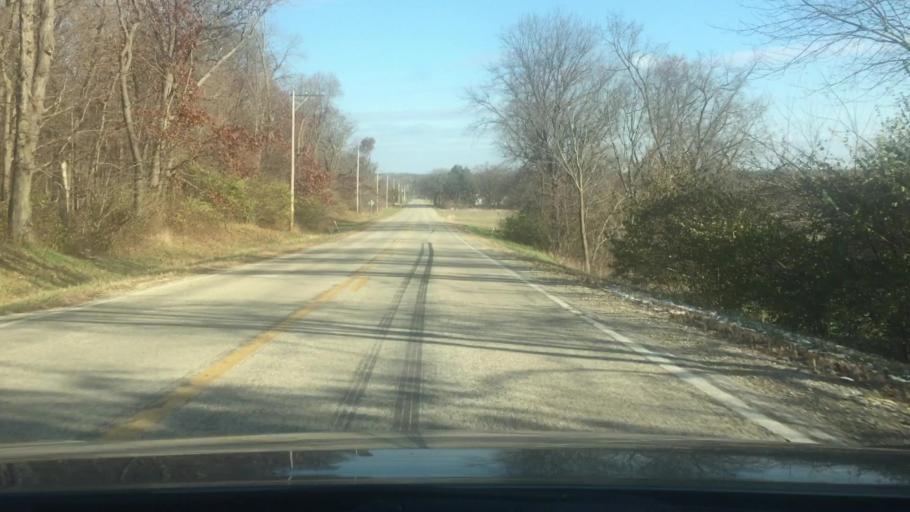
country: US
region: Wisconsin
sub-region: Jefferson County
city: Palmyra
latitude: 42.9399
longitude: -88.6048
